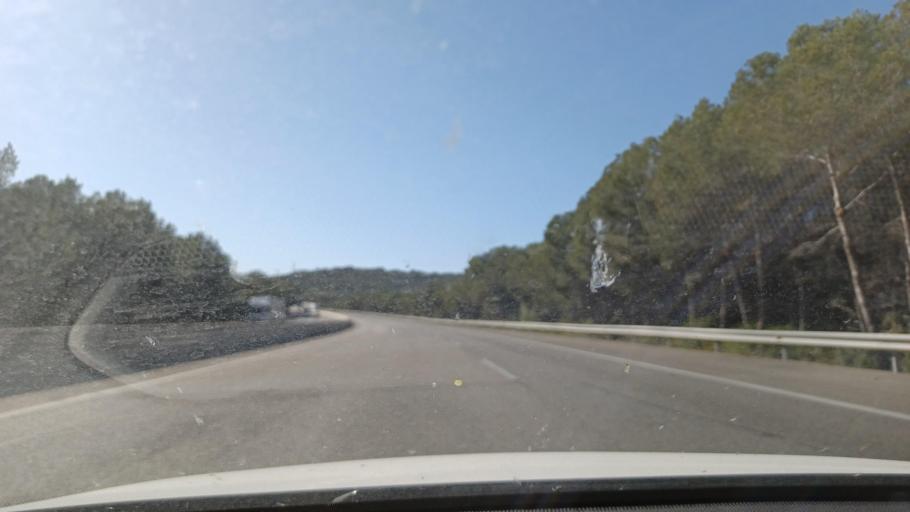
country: ES
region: Catalonia
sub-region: Provincia de Tarragona
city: el Catllar
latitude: 41.1514
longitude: 1.3020
